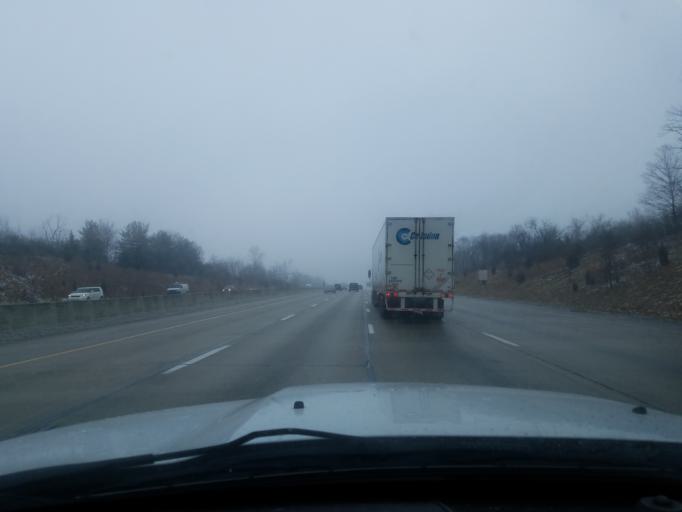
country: US
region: Indiana
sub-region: Marion County
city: Lawrence
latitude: 39.8700
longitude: -86.0471
